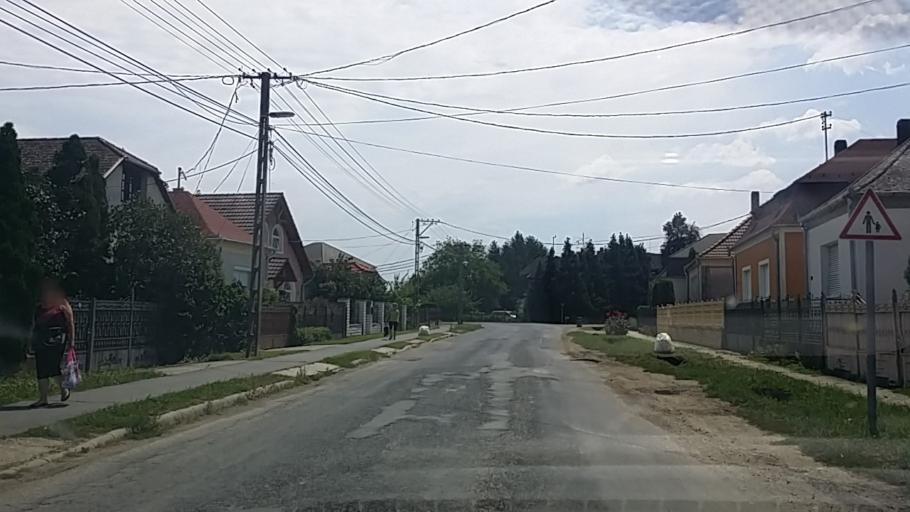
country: HR
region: Medimurska
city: Kotoriba
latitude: 46.3840
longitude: 16.8319
